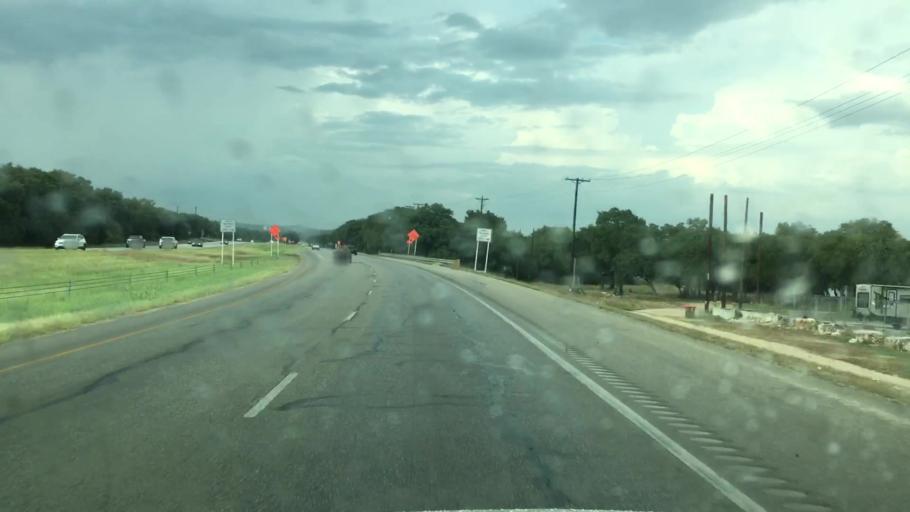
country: US
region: Texas
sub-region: Comal County
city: Bulverde
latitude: 29.8368
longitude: -98.4107
